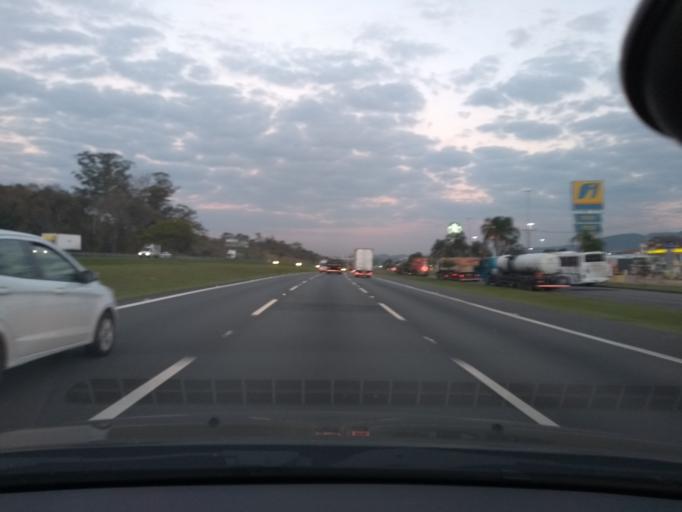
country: BR
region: Sao Paulo
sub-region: Louveira
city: Louveira
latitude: -23.1488
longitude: -46.9618
